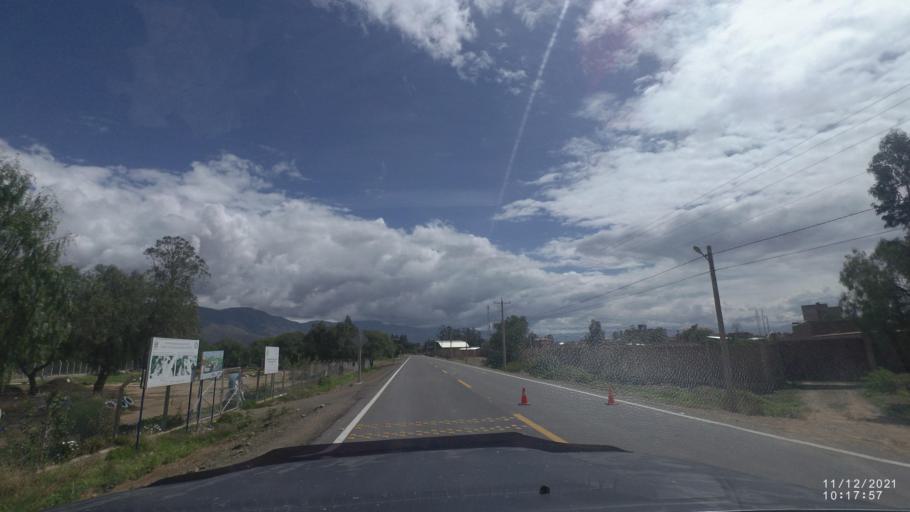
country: BO
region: Cochabamba
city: Tarata
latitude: -17.5828
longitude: -66.0186
